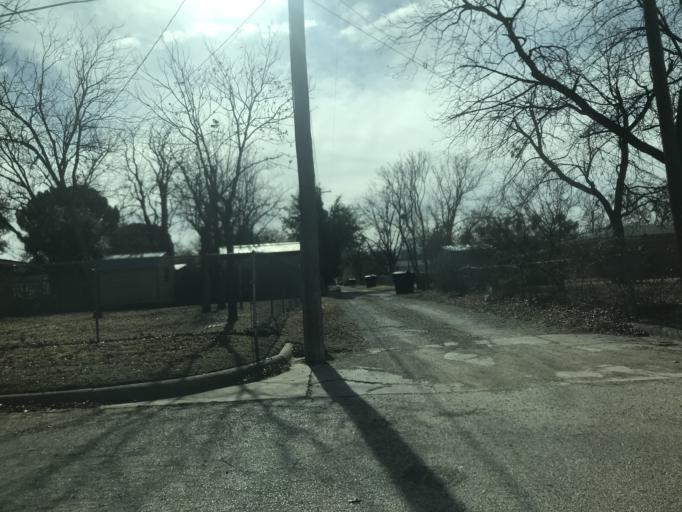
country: US
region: Texas
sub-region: Taylor County
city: Abilene
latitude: 32.4797
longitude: -99.7144
